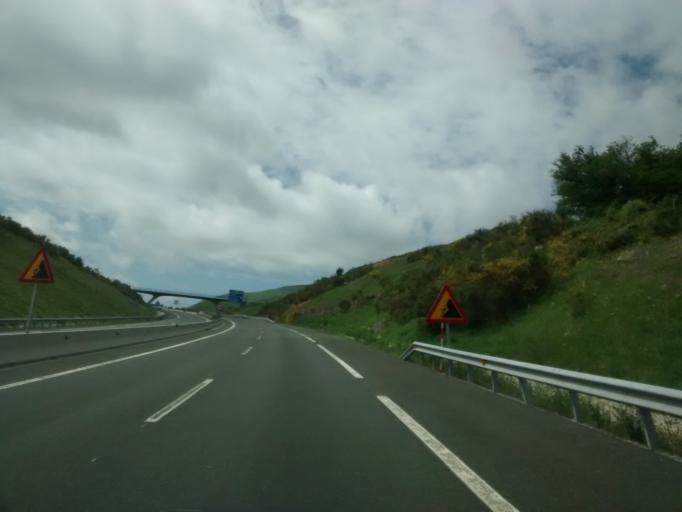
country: ES
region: Cantabria
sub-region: Provincia de Cantabria
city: Pesquera
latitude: 43.0800
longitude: -4.0860
